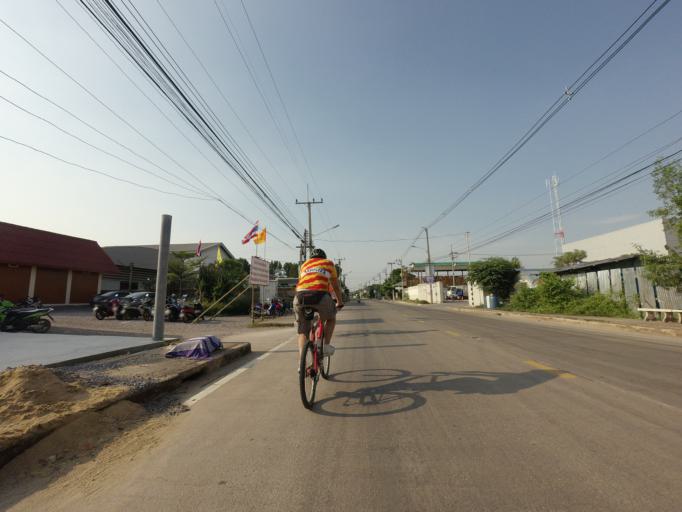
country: TH
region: Samut Sakhon
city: Samut Sakhon
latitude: 13.5226
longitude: 100.2738
